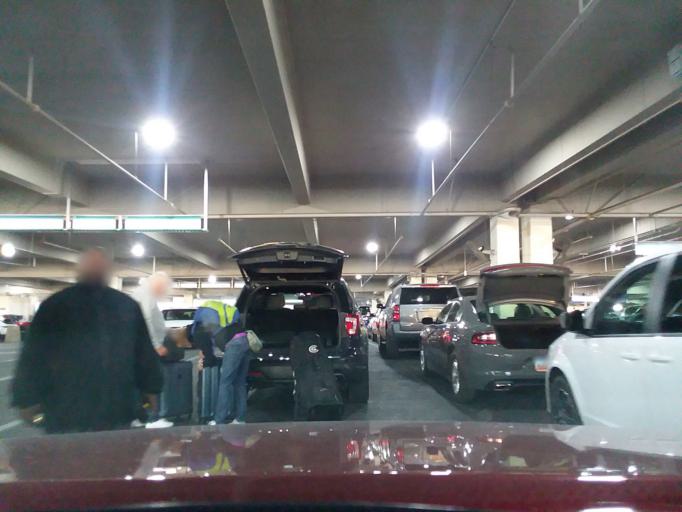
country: US
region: Nevada
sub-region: Clark County
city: Paradise
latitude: 36.0595
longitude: -115.1658
